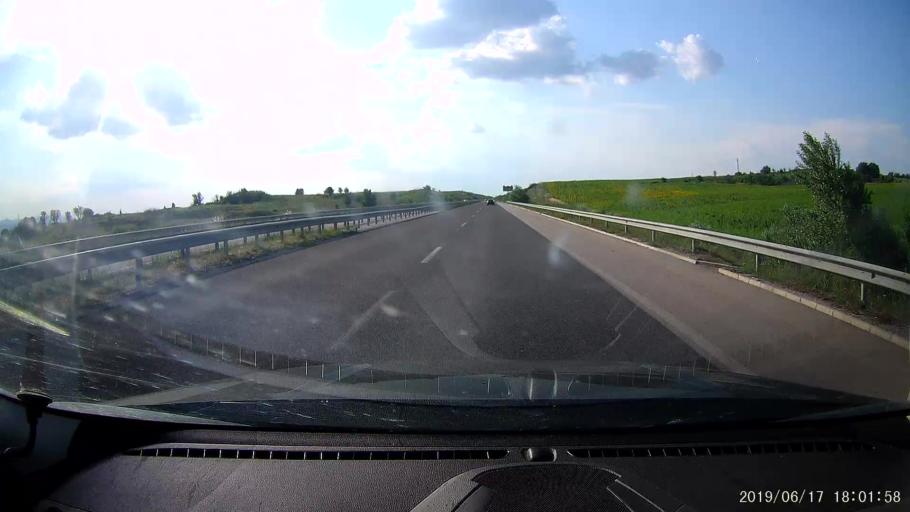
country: BG
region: Khaskovo
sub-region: Obshtina Svilengrad
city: Svilengrad
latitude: 41.7514
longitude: 26.2402
